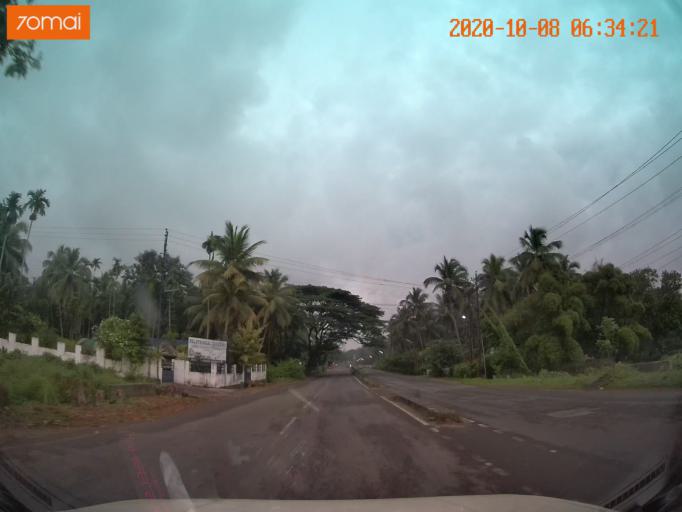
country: IN
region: Kerala
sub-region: Thrissur District
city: Avanoor
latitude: 10.5830
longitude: 76.1599
